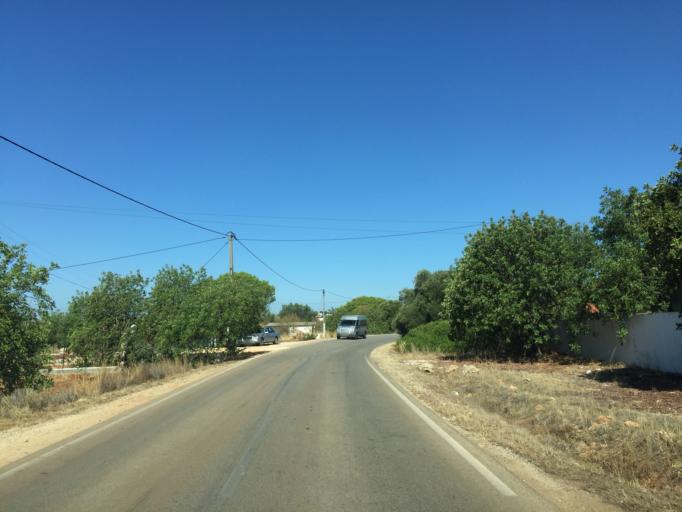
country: PT
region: Faro
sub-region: Loule
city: Vilamoura
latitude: 37.1117
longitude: -8.0734
